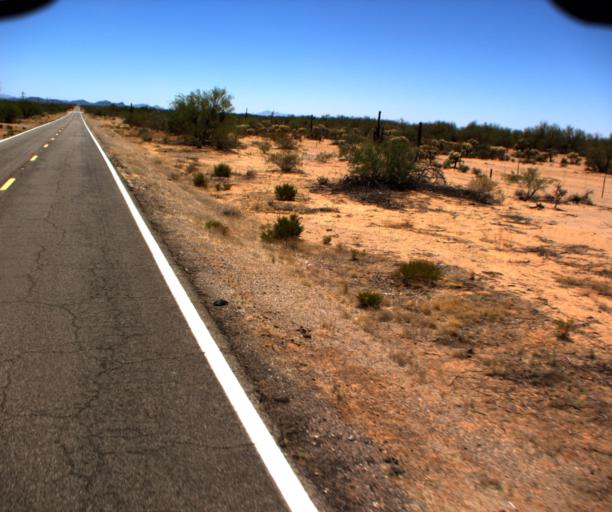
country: US
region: Arizona
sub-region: Pima County
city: Sells
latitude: 32.0944
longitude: -112.0610
